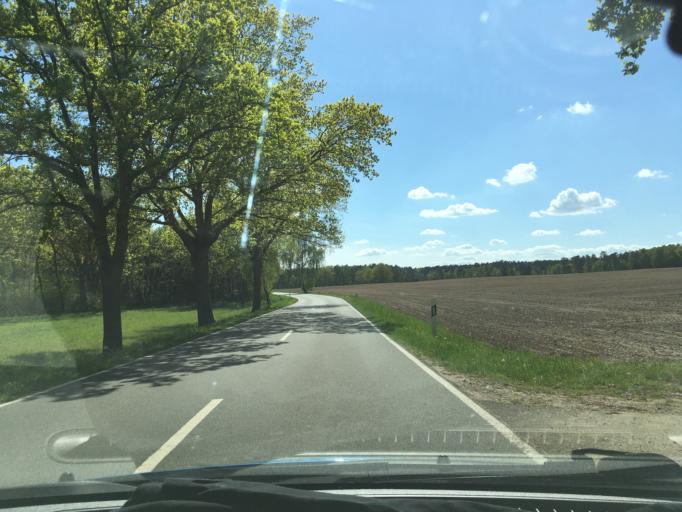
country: DE
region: Lower Saxony
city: Zernien
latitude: 53.0606
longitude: 10.8863
